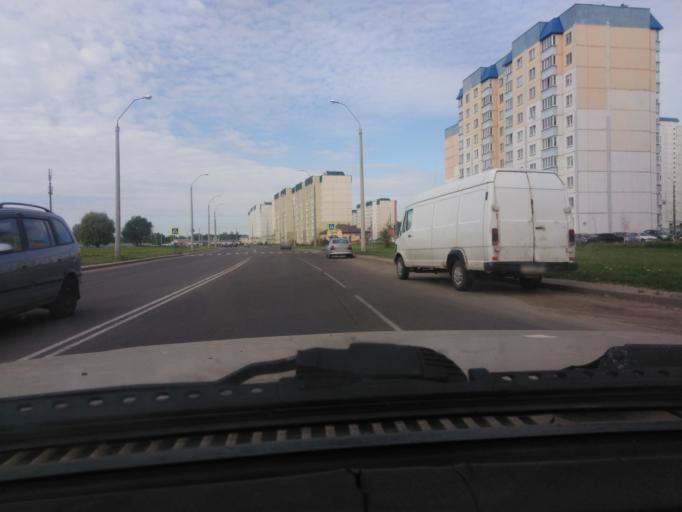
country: BY
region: Mogilev
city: Mahilyow
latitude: 53.9146
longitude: 30.2886
